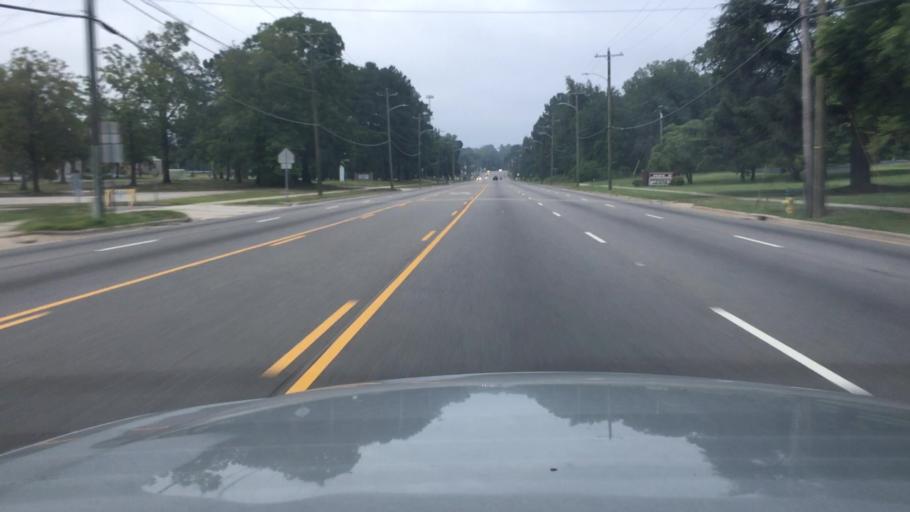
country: US
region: North Carolina
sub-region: Cumberland County
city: Fayetteville
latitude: 35.1033
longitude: -78.8782
